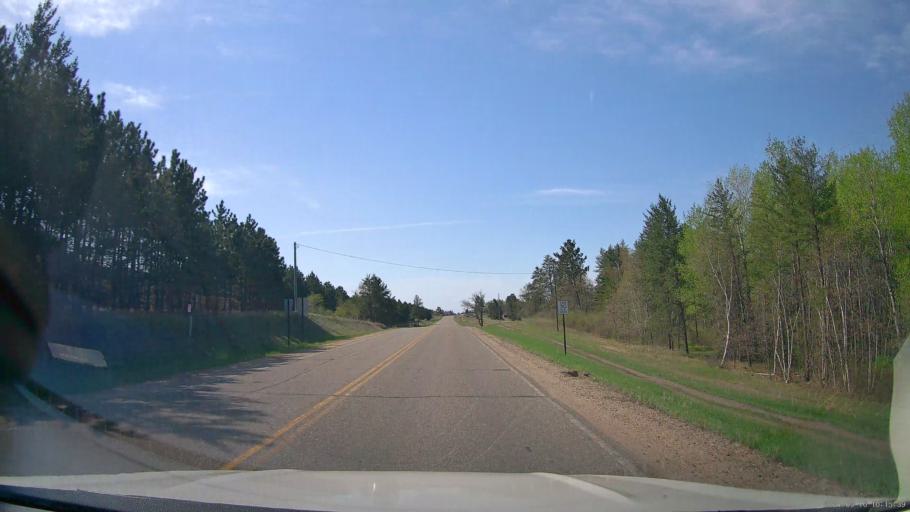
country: US
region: Minnesota
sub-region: Hubbard County
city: Park Rapids
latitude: 46.9759
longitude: -94.9527
